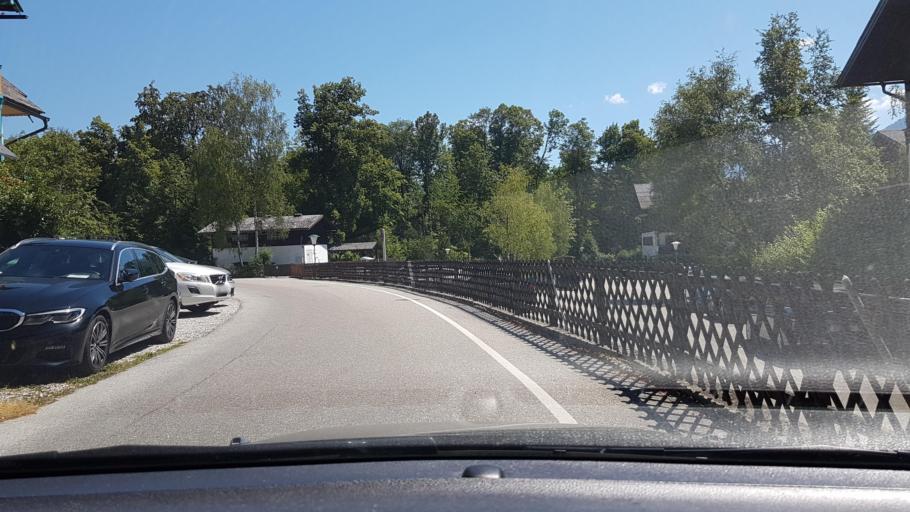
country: AT
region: Upper Austria
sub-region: Politischer Bezirk Gmunden
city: Sankt Wolfgang im Salzkammergut
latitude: 47.7420
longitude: 13.4363
